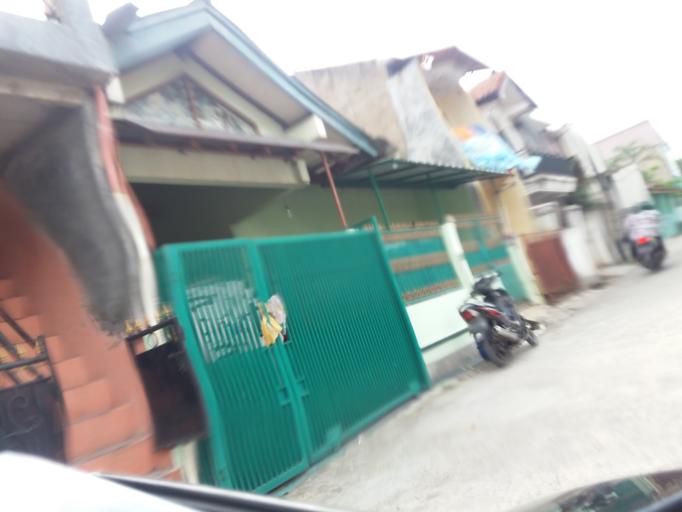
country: ID
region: West Java
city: Bandung
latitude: -6.9240
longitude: 107.6576
